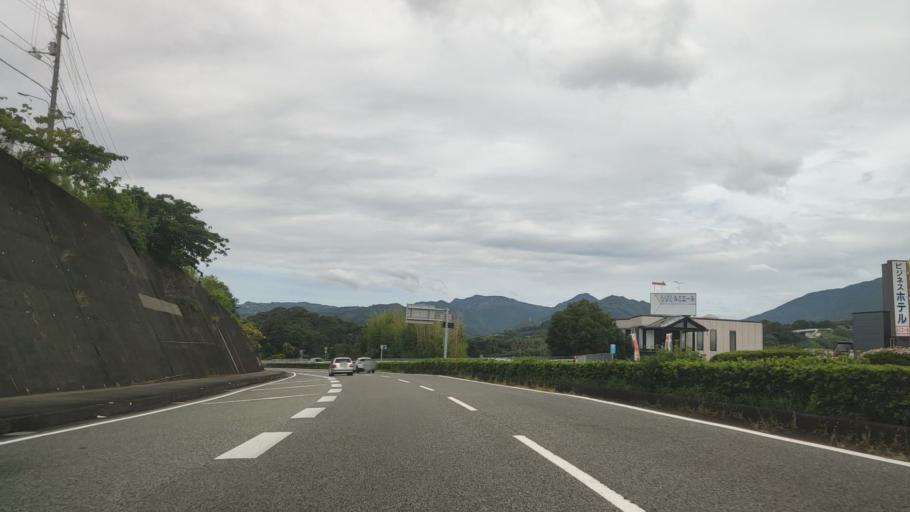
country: JP
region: Wakayama
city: Tanabe
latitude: 33.7341
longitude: 135.4006
